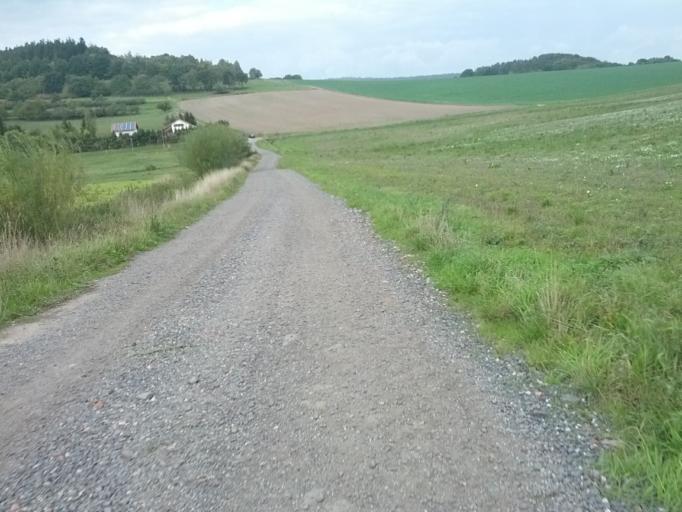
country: DE
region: Thuringia
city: Seebach
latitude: 50.9377
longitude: 10.4067
